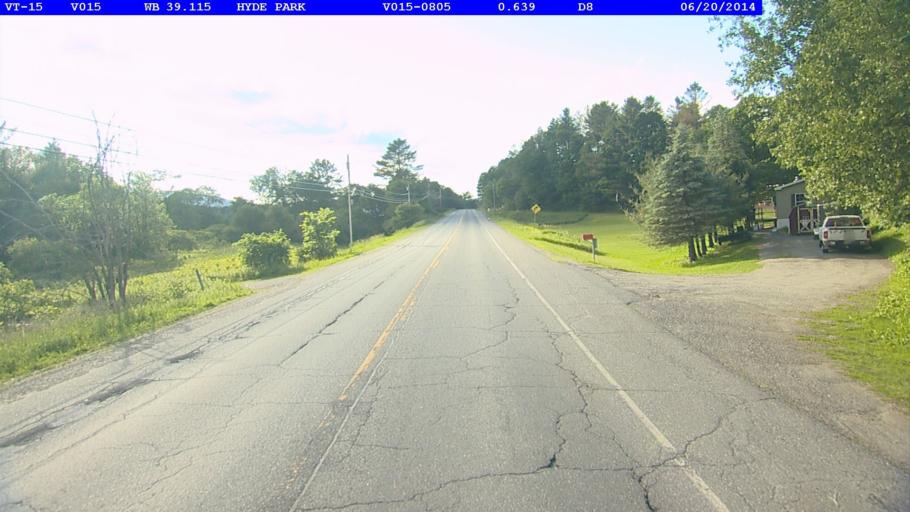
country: US
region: Vermont
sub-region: Lamoille County
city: Hyde Park
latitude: 44.6021
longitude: -72.6387
